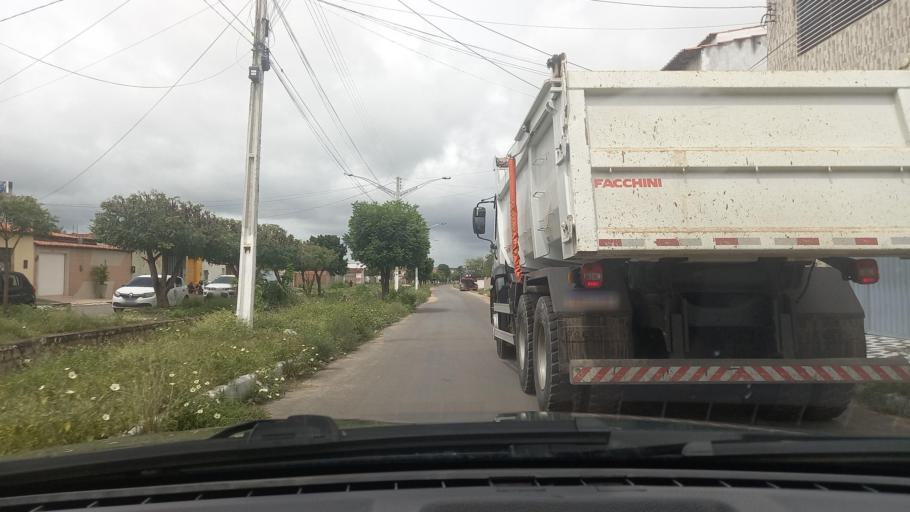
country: BR
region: Alagoas
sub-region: Delmiro Gouveia
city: Delmiro Gouveia
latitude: -9.3850
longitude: -38.0025
